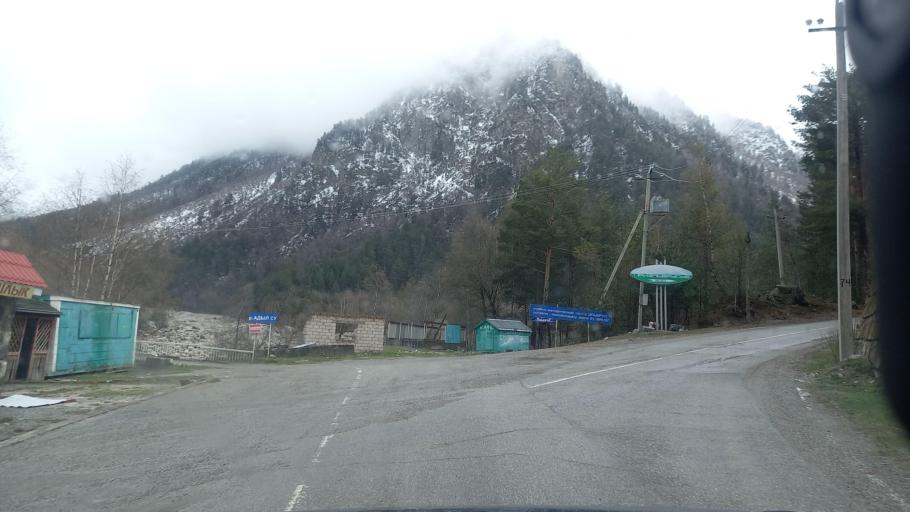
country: RU
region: Kabardino-Balkariya
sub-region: El'brusskiy Rayon
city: El'brus
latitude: 43.2285
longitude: 42.6575
